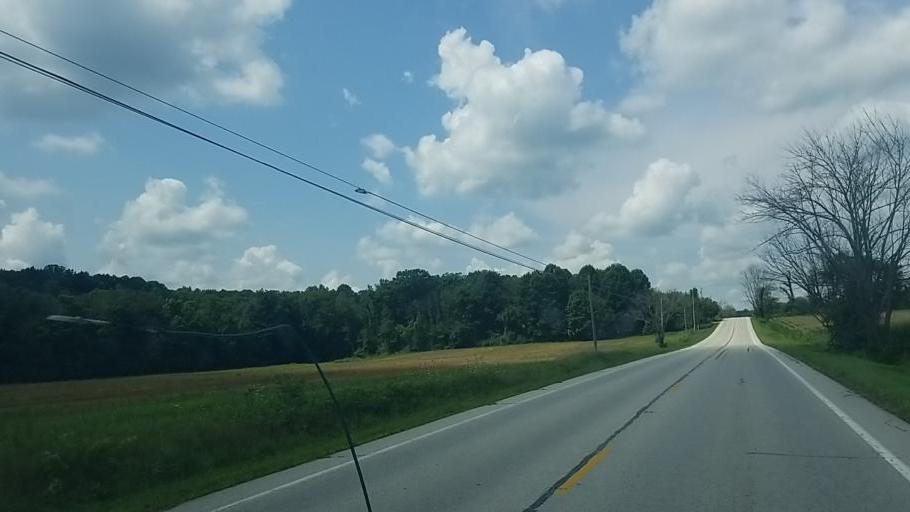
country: US
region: Ohio
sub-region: Medina County
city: Lodi
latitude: 41.0266
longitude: -82.0628
